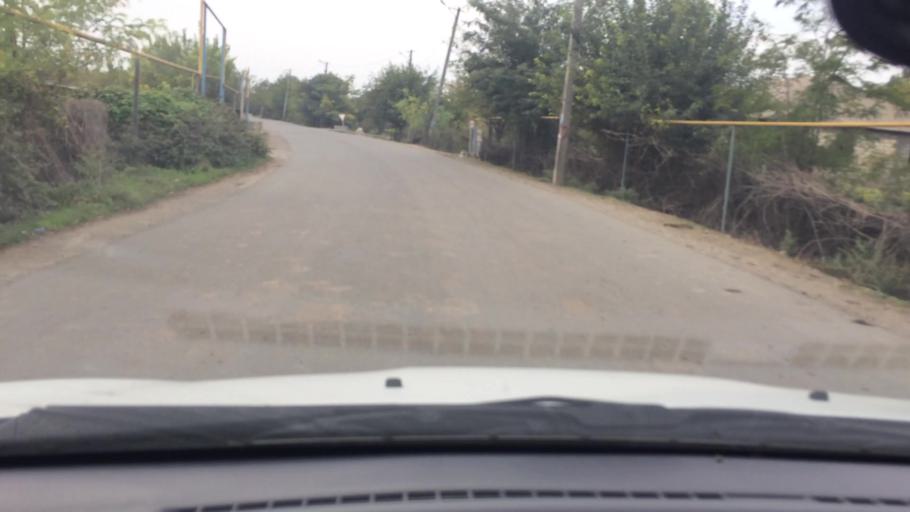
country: AM
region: Tavush
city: Berdavan
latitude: 41.3528
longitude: 44.9674
